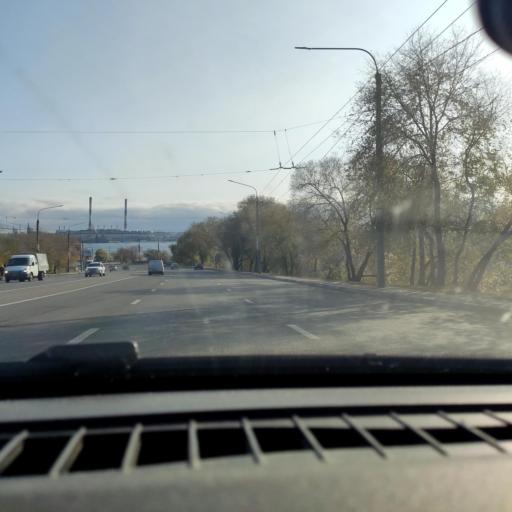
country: RU
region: Voronezj
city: Voronezh
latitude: 51.6386
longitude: 39.2064
